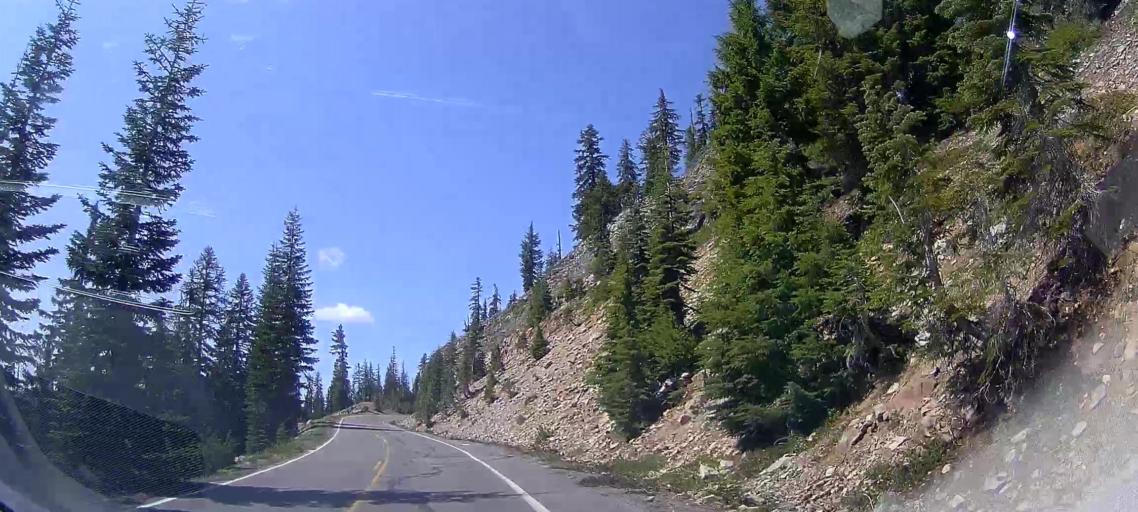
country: US
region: Oregon
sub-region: Klamath County
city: Klamath Falls
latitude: 42.8781
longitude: -122.1036
